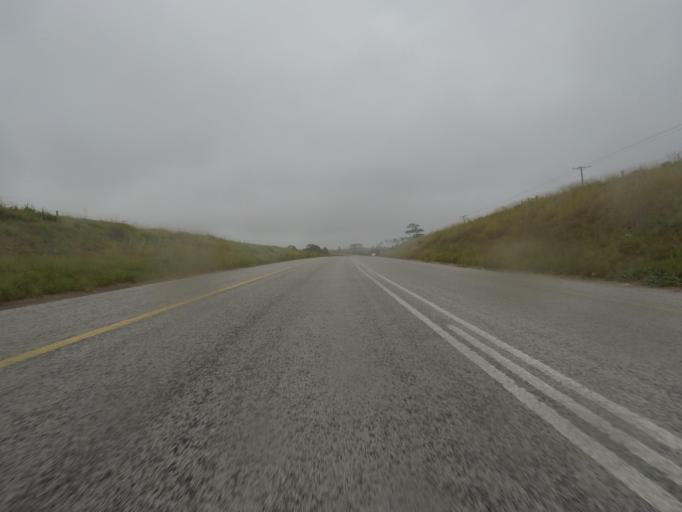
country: ZA
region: Eastern Cape
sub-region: Cacadu District Municipality
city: Grahamstown
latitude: -33.6435
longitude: 26.3502
